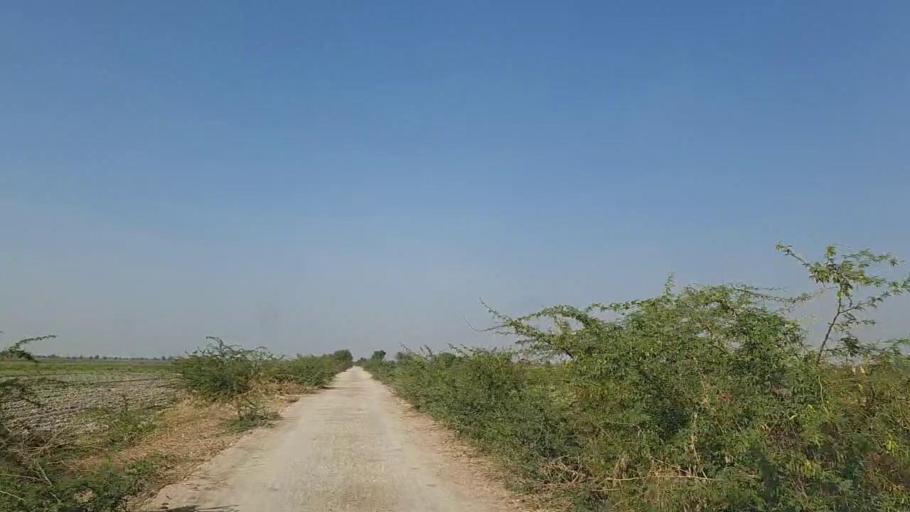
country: PK
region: Sindh
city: Naukot
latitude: 24.9092
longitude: 69.4876
